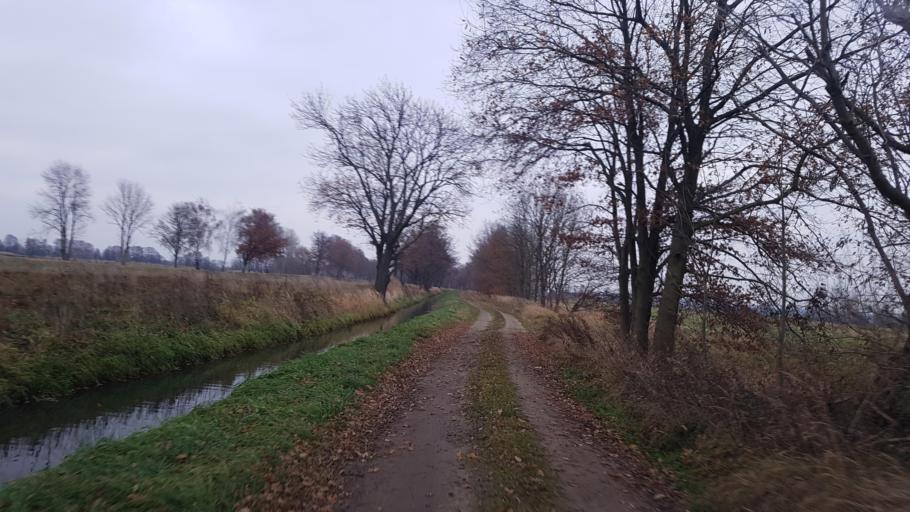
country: DE
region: Brandenburg
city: Hirschfeld
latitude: 51.4149
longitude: 13.6072
